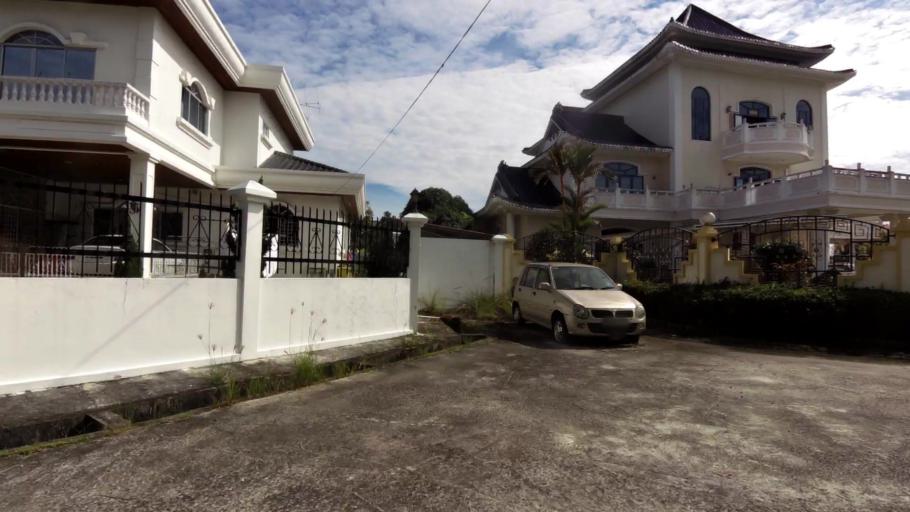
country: BN
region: Brunei and Muara
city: Bandar Seri Begawan
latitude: 4.9234
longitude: 114.9093
